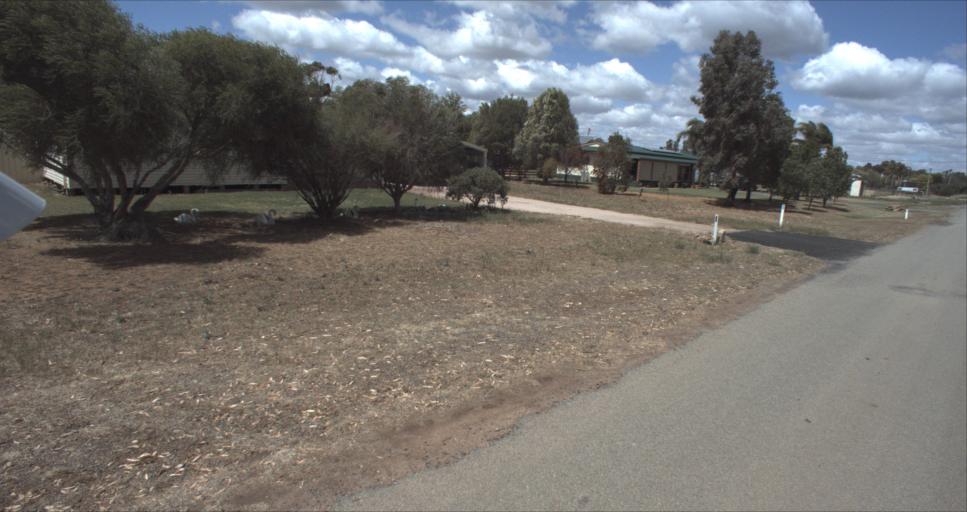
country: AU
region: New South Wales
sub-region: Murrumbidgee Shire
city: Darlington Point
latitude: -34.5134
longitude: 146.1843
